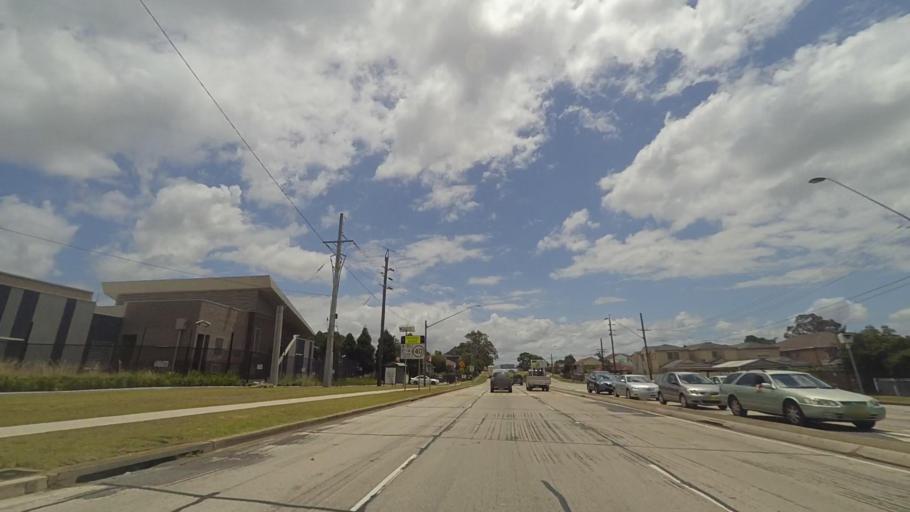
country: AU
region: New South Wales
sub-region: Fairfield
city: Cabramatta West
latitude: -33.8882
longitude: 150.9228
